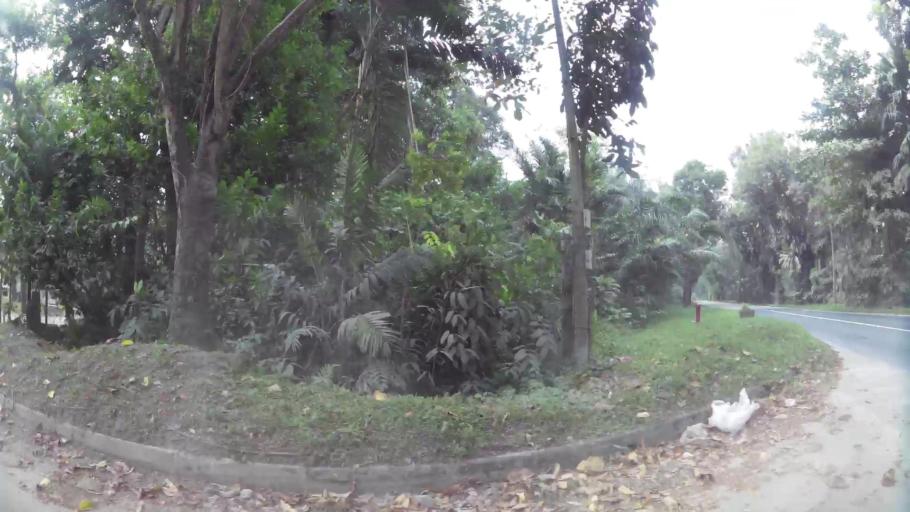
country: MY
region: Johor
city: Johor Bahru
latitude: 1.4381
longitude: 103.7080
